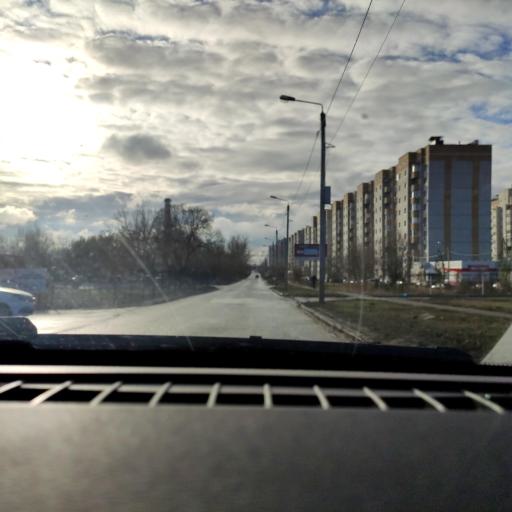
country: RU
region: Voronezj
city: Somovo
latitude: 51.6771
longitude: 39.2910
